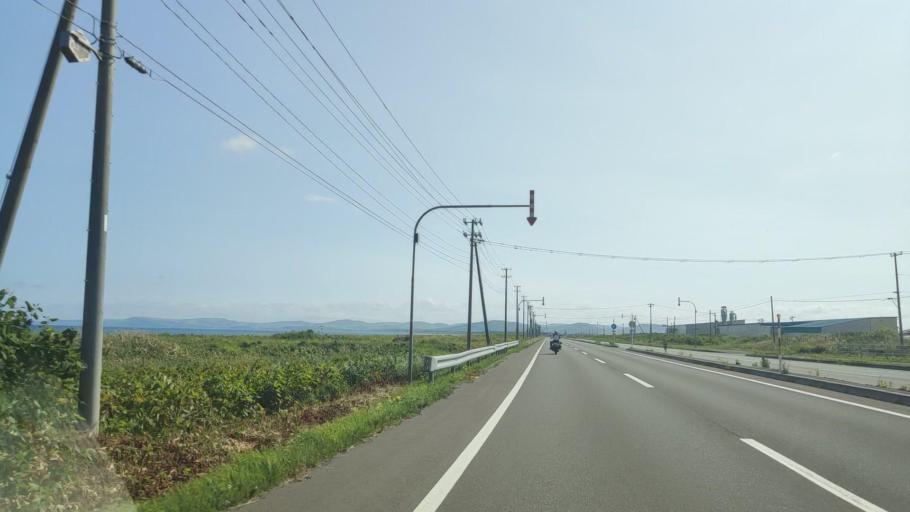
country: JP
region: Hokkaido
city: Makubetsu
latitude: 45.4032
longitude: 141.7851
